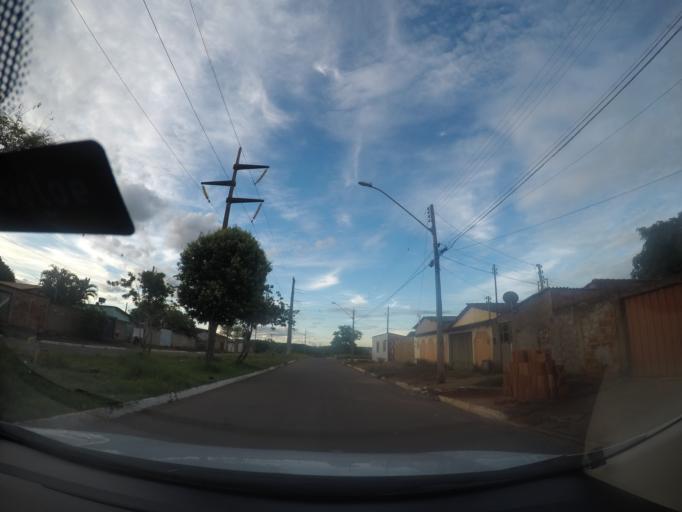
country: BR
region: Goias
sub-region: Goianira
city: Goianira
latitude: -16.5861
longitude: -49.3773
